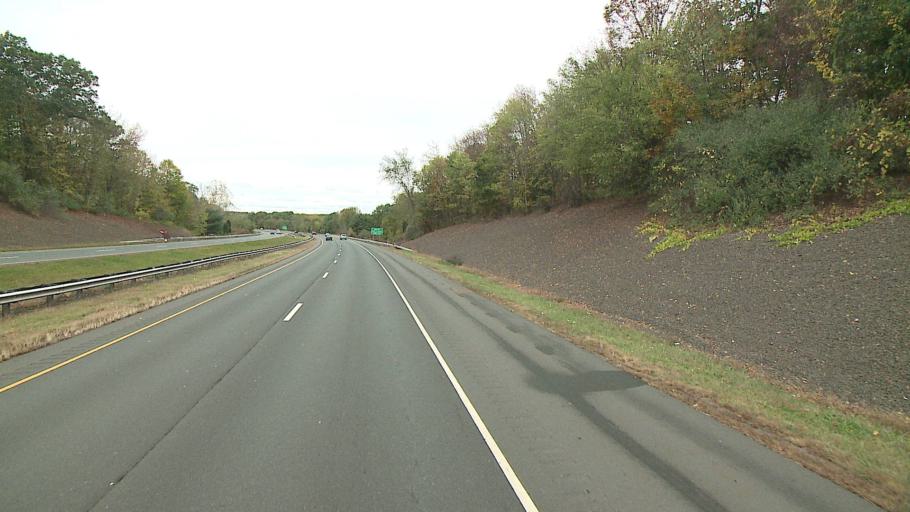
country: US
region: Connecticut
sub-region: Hartford County
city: Kensington
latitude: 41.6257
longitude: -72.7127
